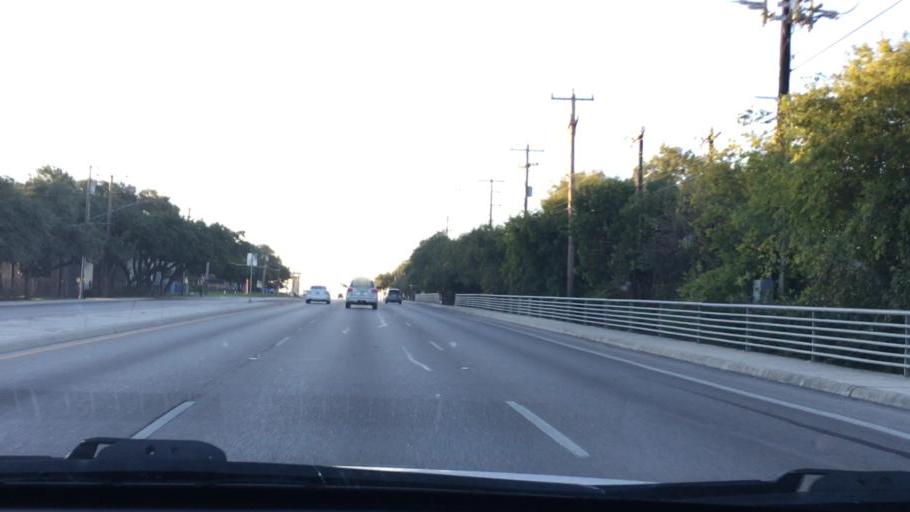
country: US
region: Texas
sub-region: Bexar County
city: Castle Hills
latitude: 29.5479
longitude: -98.5309
